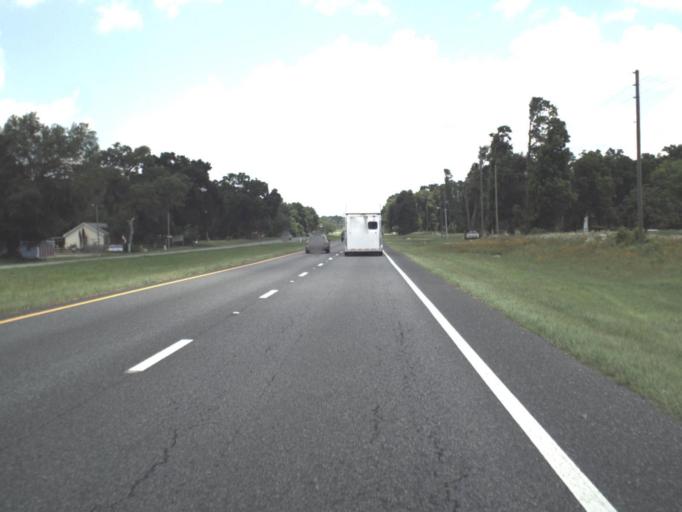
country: US
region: Florida
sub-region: Alachua County
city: High Springs
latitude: 29.8147
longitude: -82.5685
